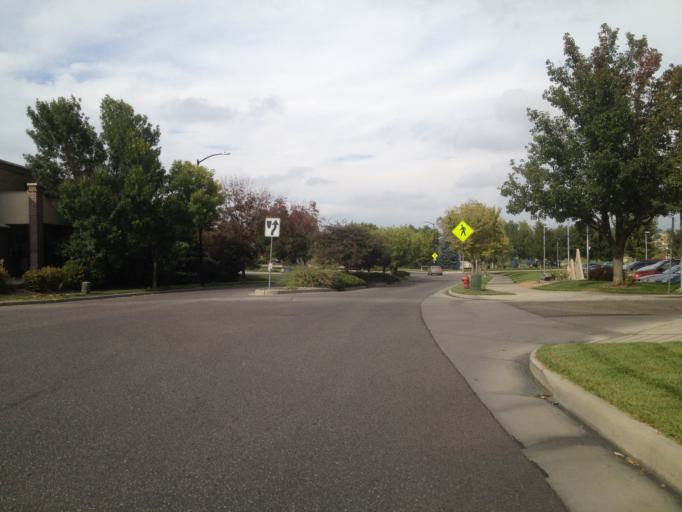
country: US
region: Colorado
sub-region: Boulder County
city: Lafayette
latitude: 40.0007
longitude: -105.1004
